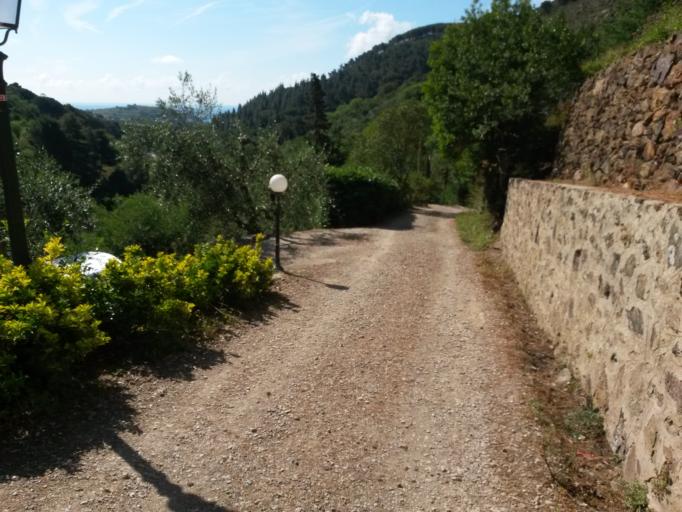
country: IT
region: Tuscany
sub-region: Provincia di Livorno
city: Porto Azzurro
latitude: 42.7831
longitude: 10.3933
